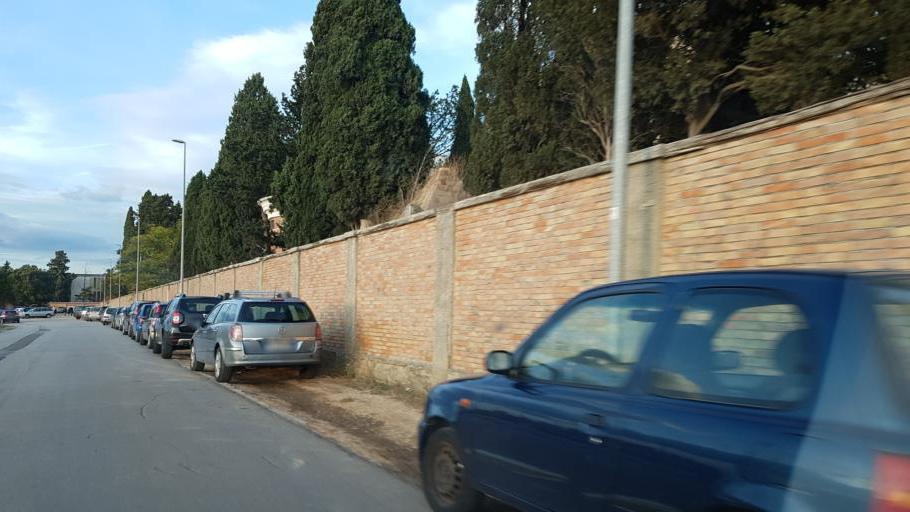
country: IT
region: Apulia
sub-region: Provincia di Foggia
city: Foggia
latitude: 41.4747
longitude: 15.5472
